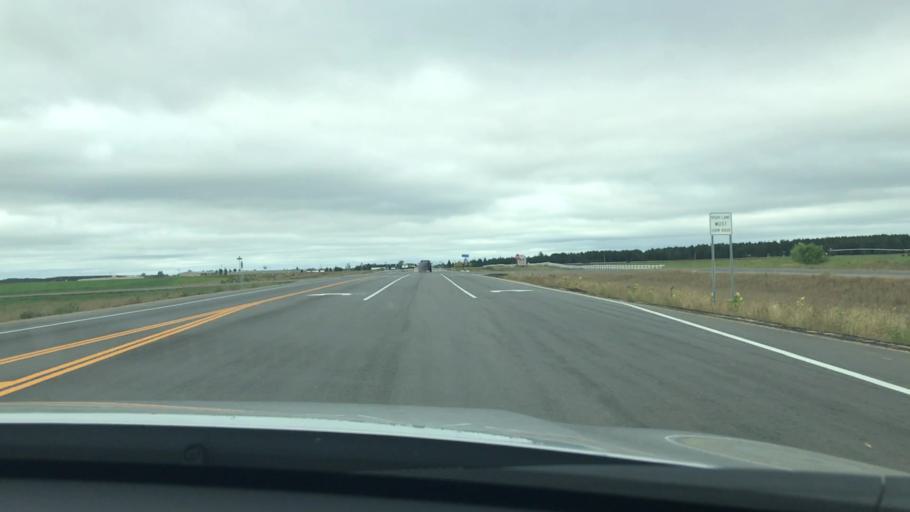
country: US
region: Minnesota
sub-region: Hubbard County
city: Park Rapids
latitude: 46.8874
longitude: -95.0631
